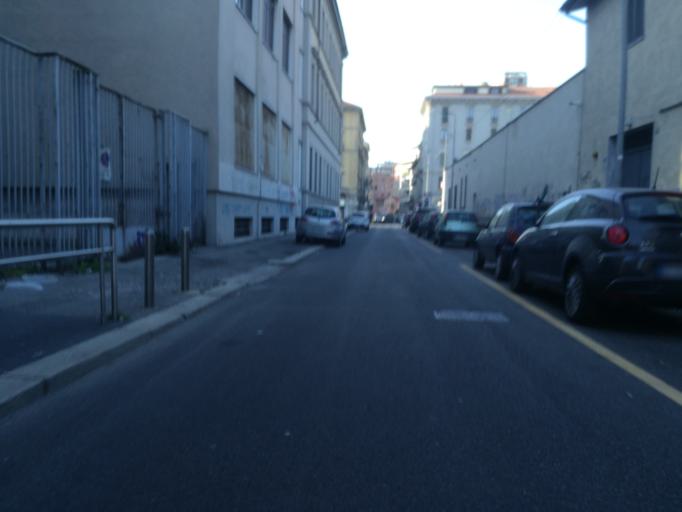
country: IT
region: Lombardy
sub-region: Citta metropolitana di Milano
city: Milano
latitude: 45.4479
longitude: 9.2004
